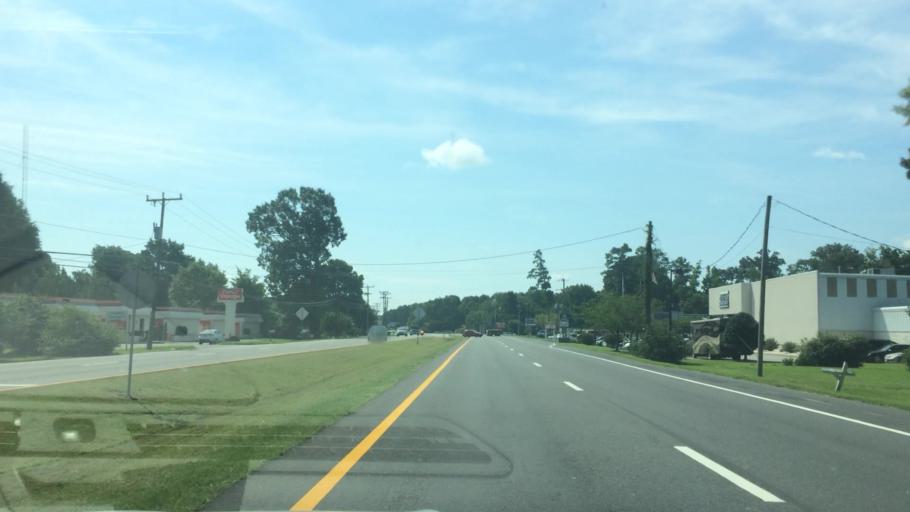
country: US
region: Virginia
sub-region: York County
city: Yorktown
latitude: 37.1834
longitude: -76.4837
